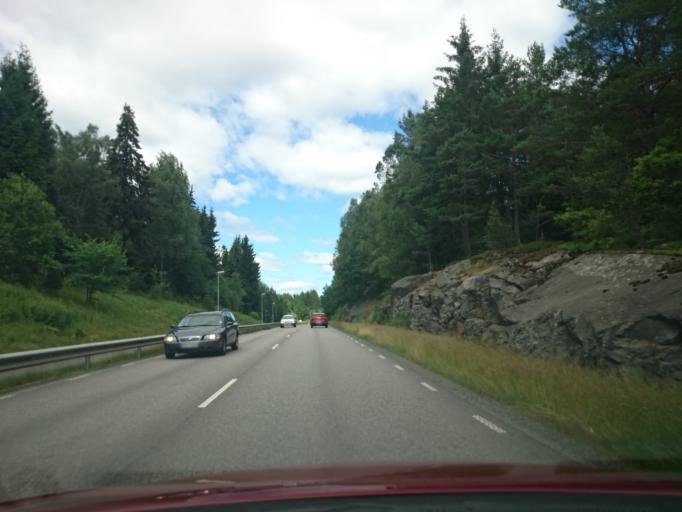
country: SE
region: Vaestra Goetaland
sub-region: Lerums Kommun
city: Grabo
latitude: 57.8226
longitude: 12.2959
